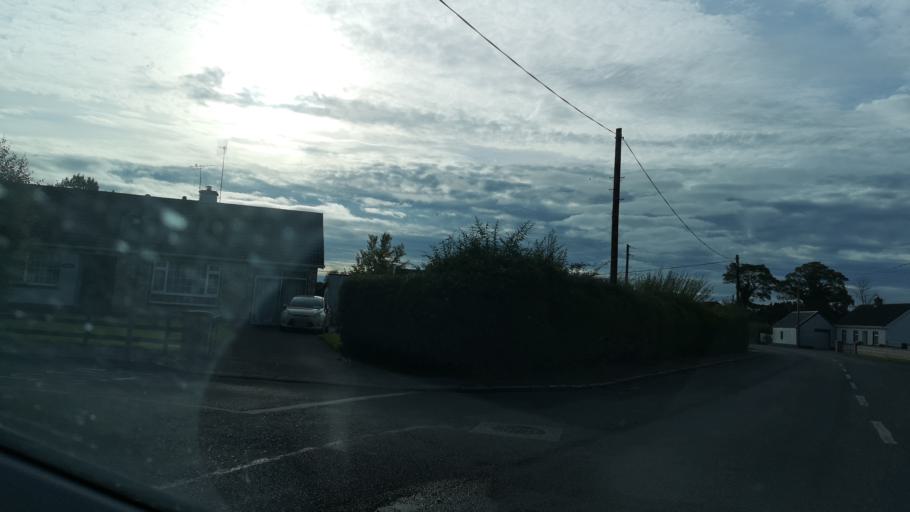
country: IE
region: Connaught
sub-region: County Galway
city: Ballinasloe
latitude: 53.3416
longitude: -8.2485
